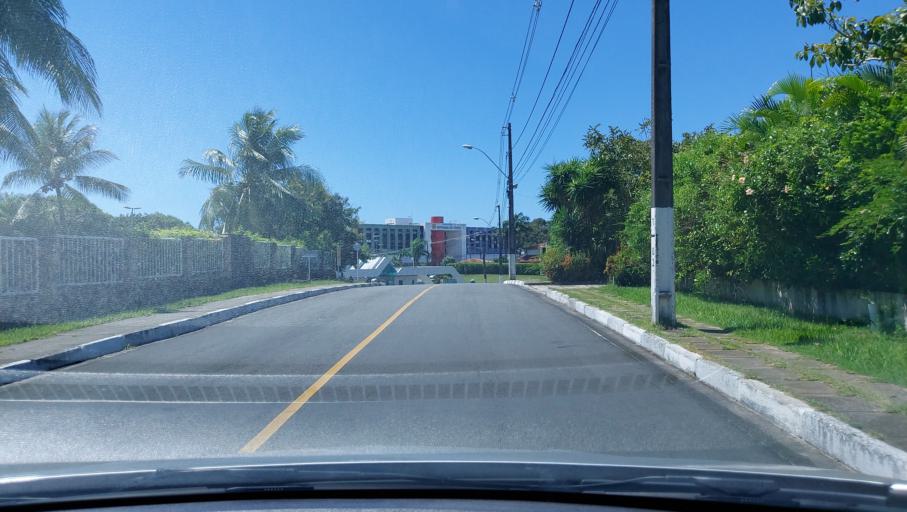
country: BR
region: Bahia
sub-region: Lauro De Freitas
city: Lauro de Freitas
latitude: -12.8731
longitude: -38.3065
